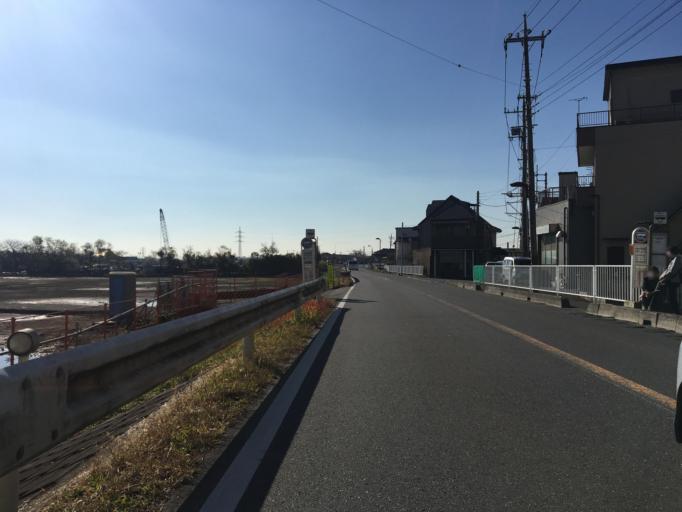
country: JP
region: Saitama
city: Yashio-shi
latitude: 35.8065
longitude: 139.8551
